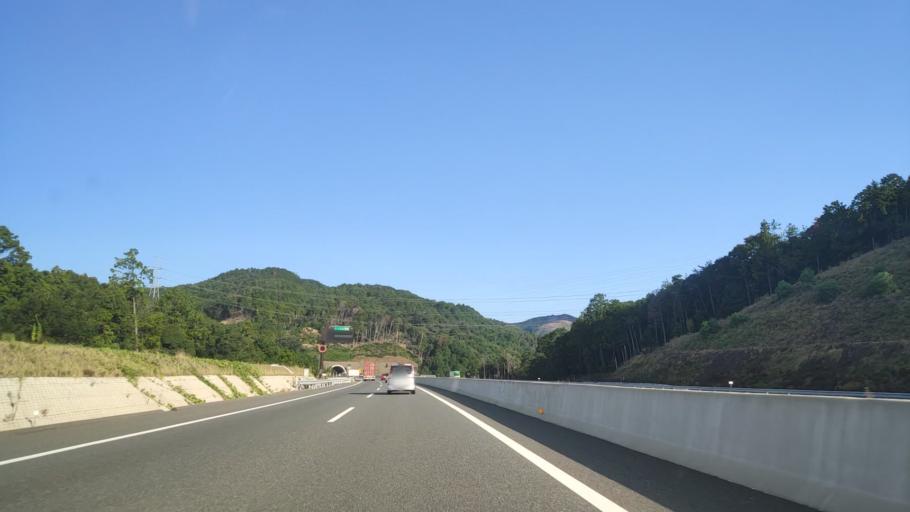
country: JP
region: Osaka
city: Takatsuki
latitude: 34.8993
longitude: 135.6042
